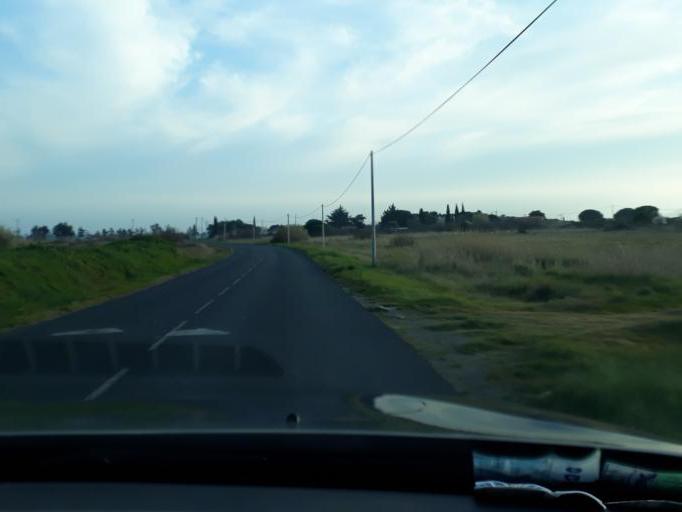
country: FR
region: Languedoc-Roussillon
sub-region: Departement de l'Herault
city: Marseillan
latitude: 43.3335
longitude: 3.5316
